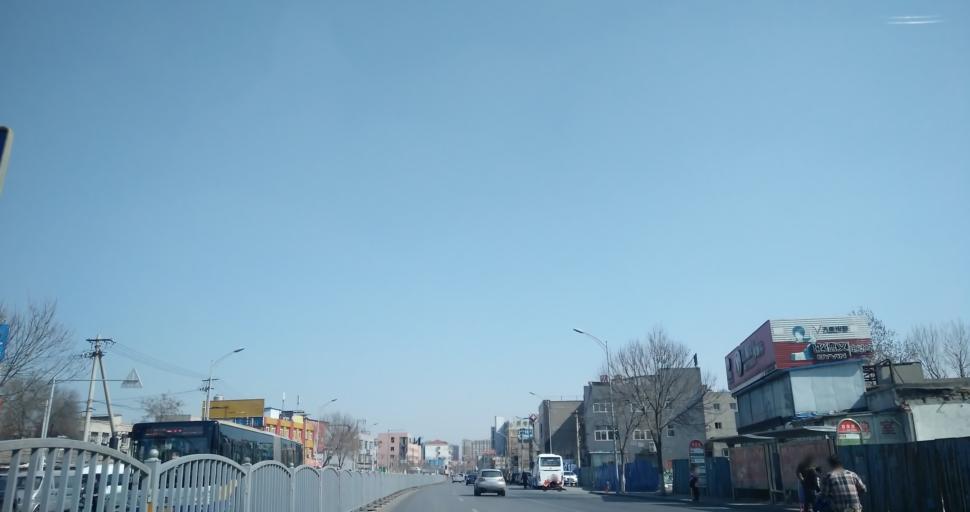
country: CN
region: Beijing
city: Jiugong
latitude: 39.8032
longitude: 116.4302
